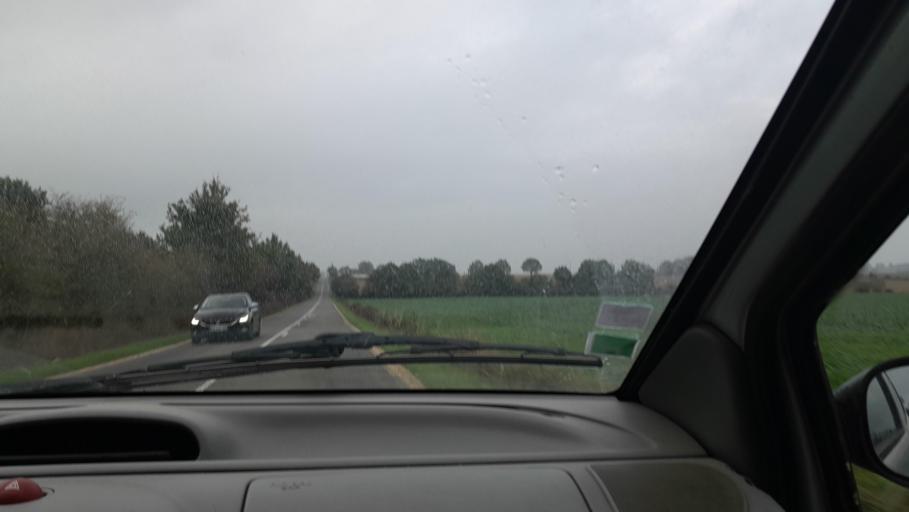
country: FR
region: Pays de la Loire
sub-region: Departement de la Mayenne
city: Congrier
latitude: 47.8100
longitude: -1.1489
